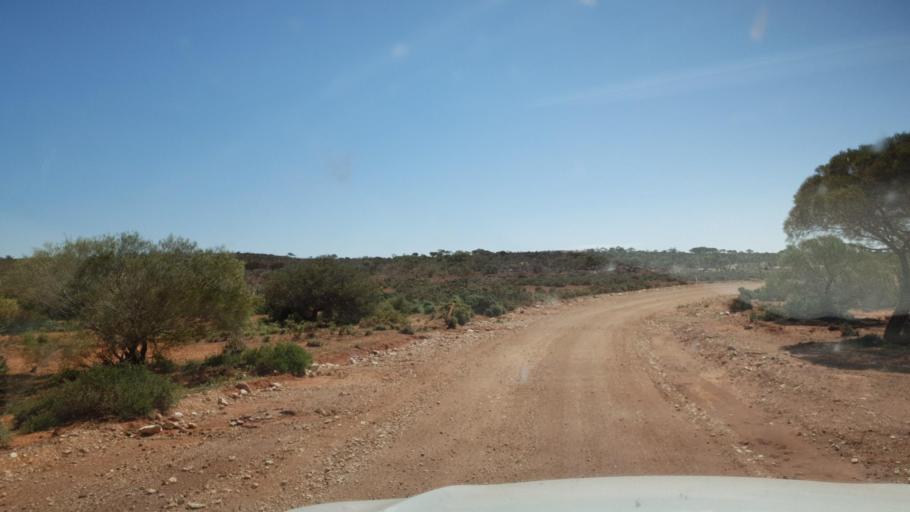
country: AU
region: South Australia
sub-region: Kimba
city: Caralue
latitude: -32.5166
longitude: 136.4949
